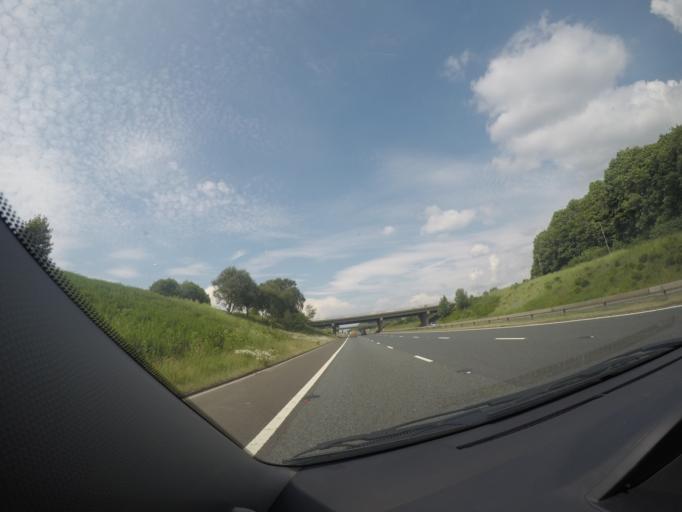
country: GB
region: England
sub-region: Cumbria
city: Scotby
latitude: 54.8558
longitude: -2.8792
